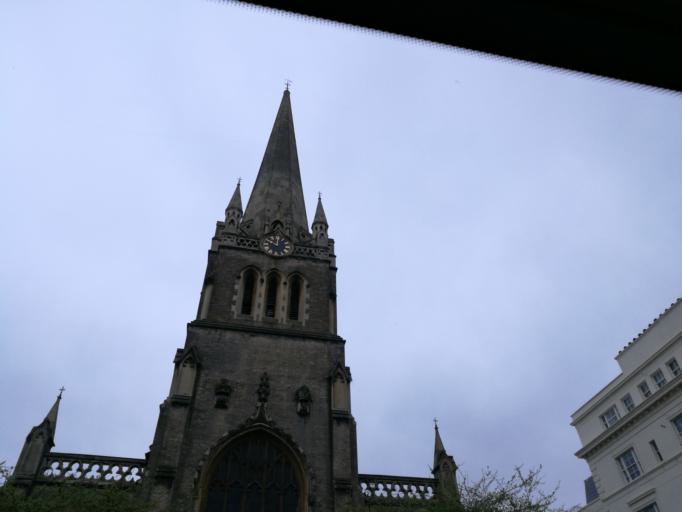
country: GB
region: England
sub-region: Greater London
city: Bayswater
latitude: 51.5132
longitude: -0.1761
